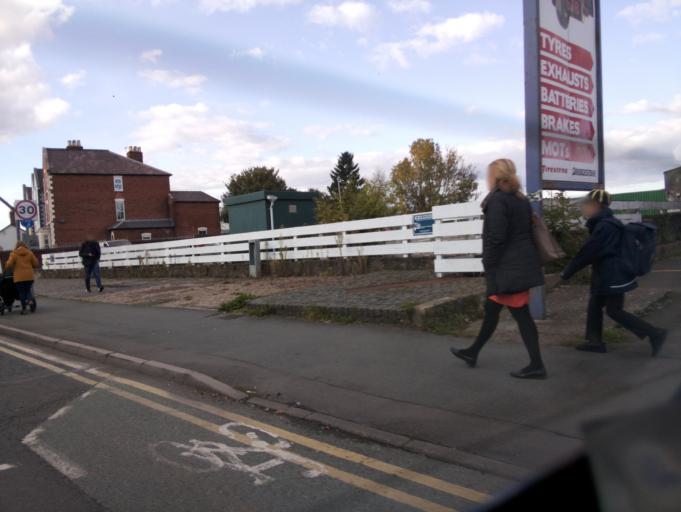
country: GB
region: England
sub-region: Herefordshire
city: Hereford
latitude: 52.0575
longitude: -2.7253
